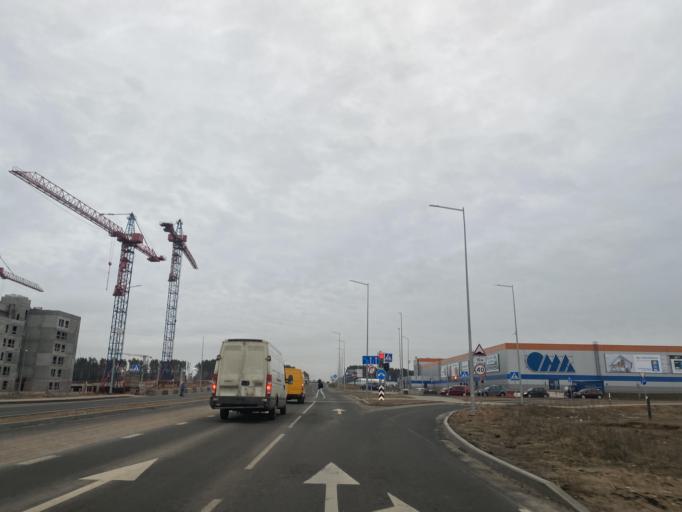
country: BY
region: Minsk
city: Borovlyany
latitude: 53.9685
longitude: 27.6221
